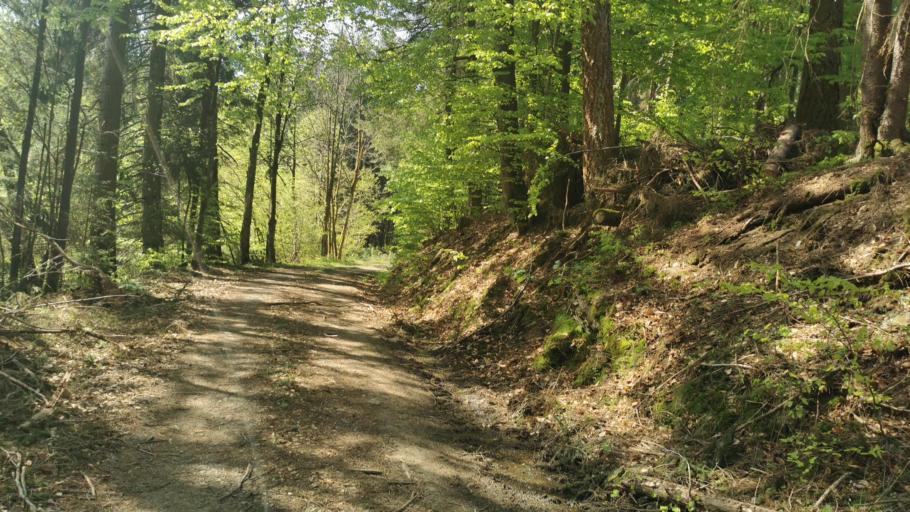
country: DE
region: Bavaria
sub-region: Upper Franconia
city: Nordhalben
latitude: 50.4096
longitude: 11.5035
